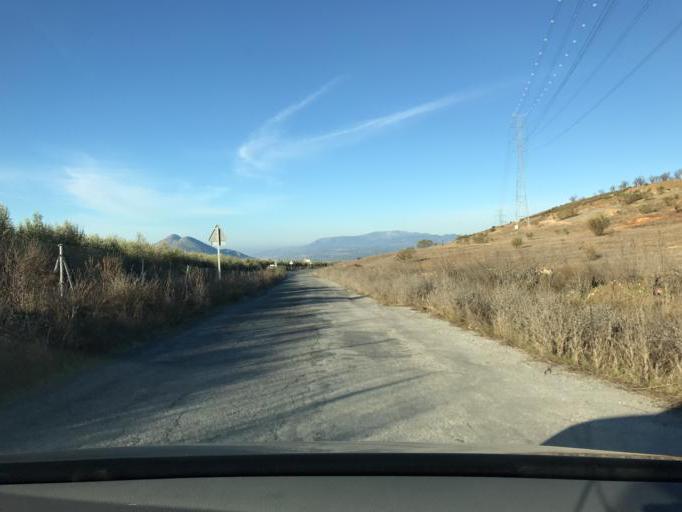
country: ES
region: Andalusia
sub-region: Provincia de Granada
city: Calicasas
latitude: 37.2610
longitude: -3.6241
